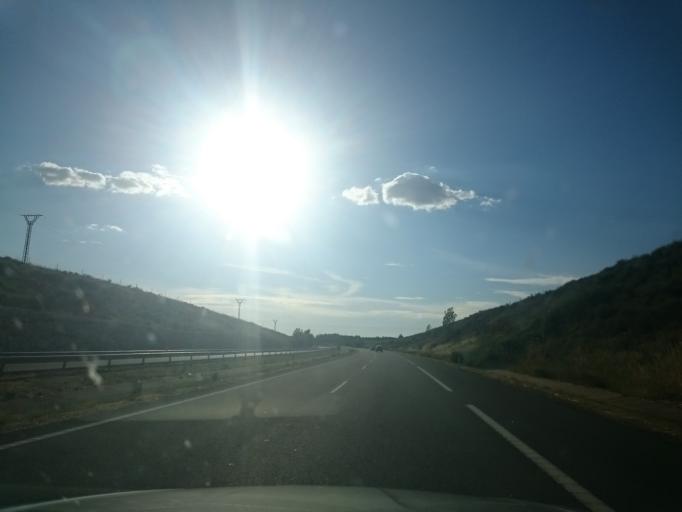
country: ES
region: Castille and Leon
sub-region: Provincia de Burgos
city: Melgar de Fernamental
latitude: 42.4098
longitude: -4.2376
